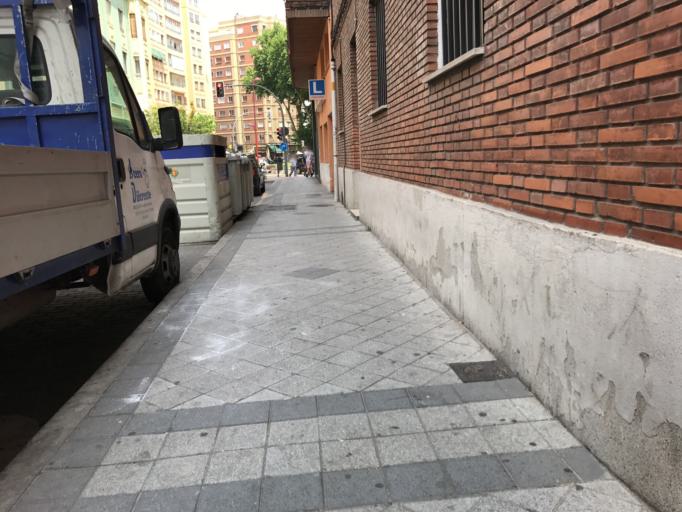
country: ES
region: Castille and Leon
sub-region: Provincia de Valladolid
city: Valladolid
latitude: 41.6464
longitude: -4.7176
